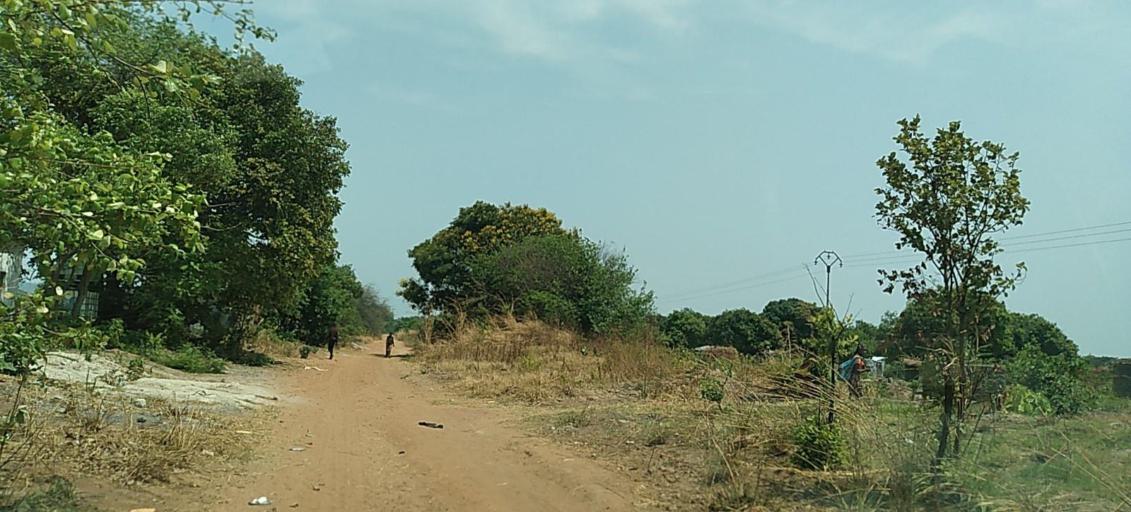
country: ZM
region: Copperbelt
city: Ndola
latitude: -13.0635
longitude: 28.7400
